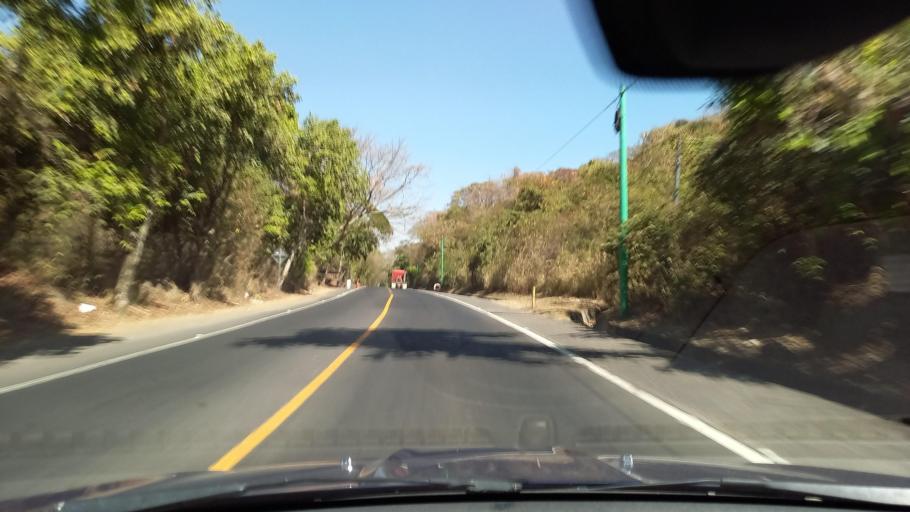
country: SV
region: Santa Ana
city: Santa Ana
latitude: 13.9924
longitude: -89.5415
